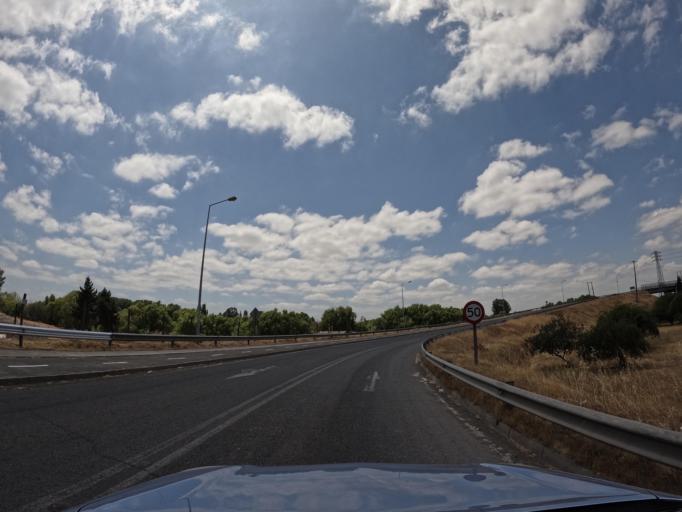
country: CL
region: Maule
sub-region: Provincia de Curico
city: Curico
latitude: -35.0008
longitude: -71.2390
